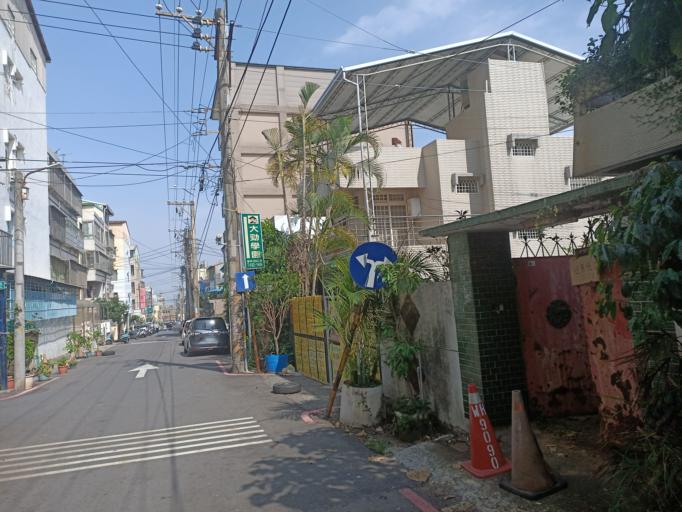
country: TW
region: Taiwan
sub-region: Taichung City
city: Taichung
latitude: 24.1875
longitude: 120.5923
